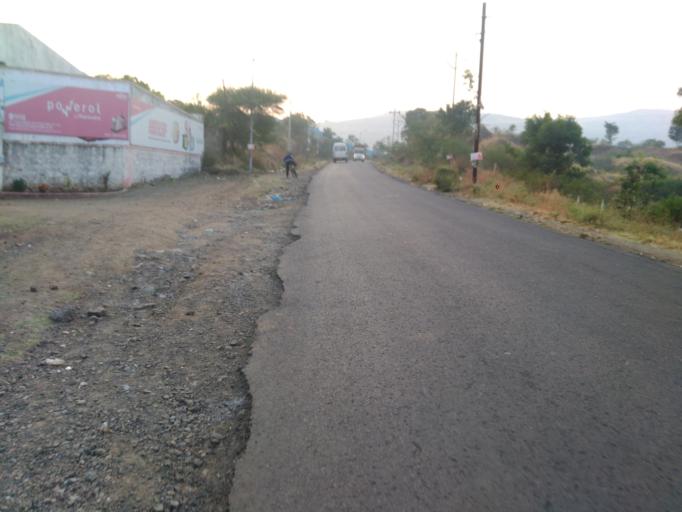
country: IN
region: Maharashtra
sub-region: Pune Division
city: Pune
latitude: 18.4266
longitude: 73.9011
